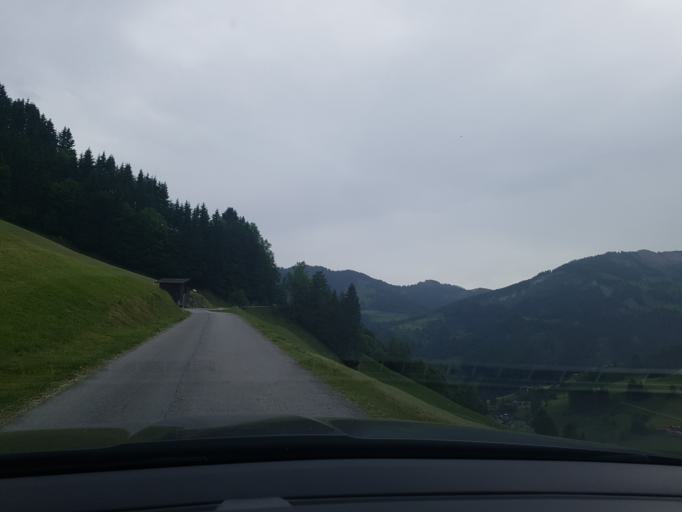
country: AT
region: Salzburg
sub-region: Politischer Bezirk Sankt Johann im Pongau
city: Schwarzach im Pongau
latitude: 47.2719
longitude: 13.2039
